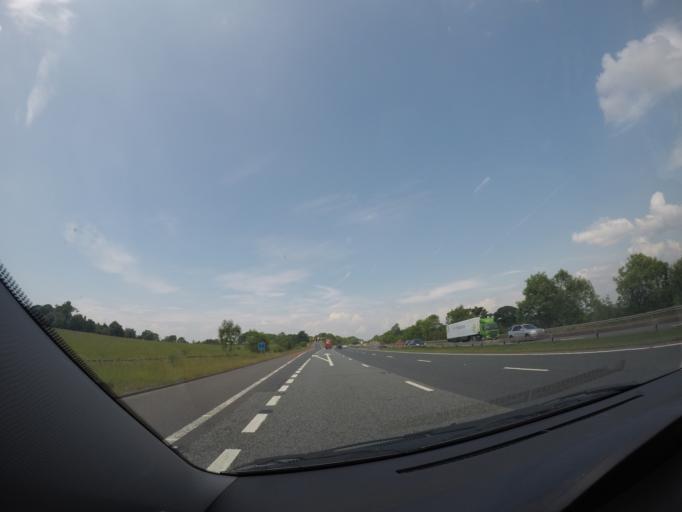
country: GB
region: England
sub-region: Cumbria
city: Scotby
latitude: 54.7928
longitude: -2.8682
